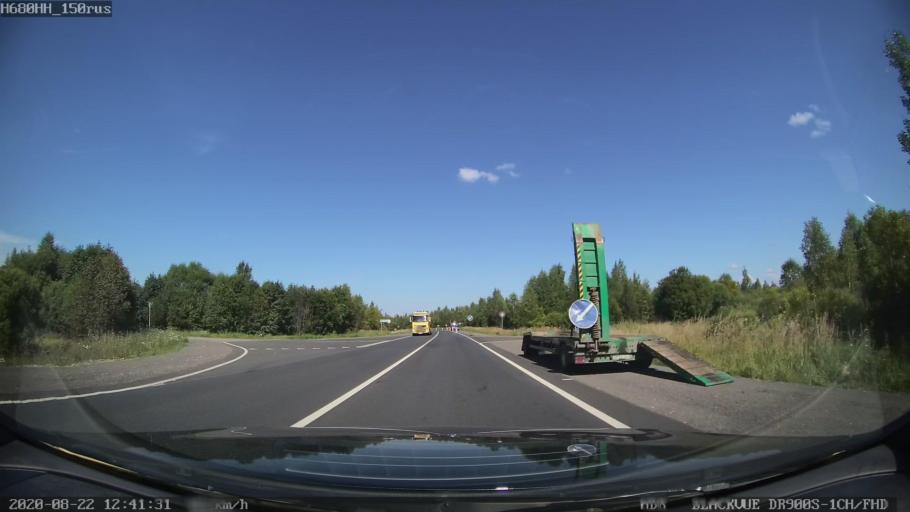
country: RU
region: Tverskaya
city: Rameshki
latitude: 57.3502
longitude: 36.0993
